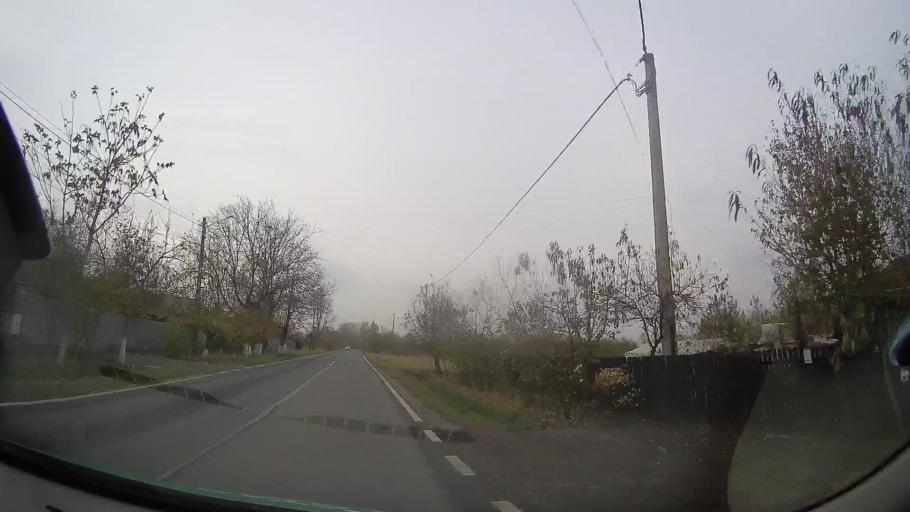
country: RO
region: Ilfov
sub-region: Comuna Gruiu
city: Silistea Snagovului
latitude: 44.7492
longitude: 26.1966
